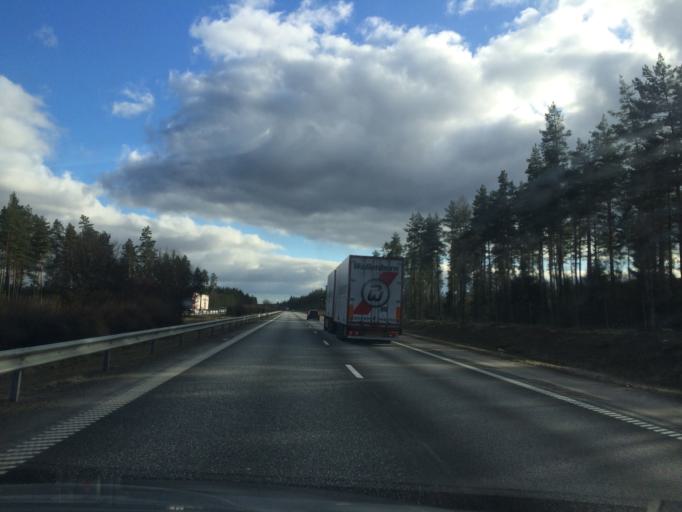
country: SE
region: Joenkoeping
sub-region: Vaggeryds Kommun
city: Skillingaryd
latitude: 57.3940
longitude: 14.0995
